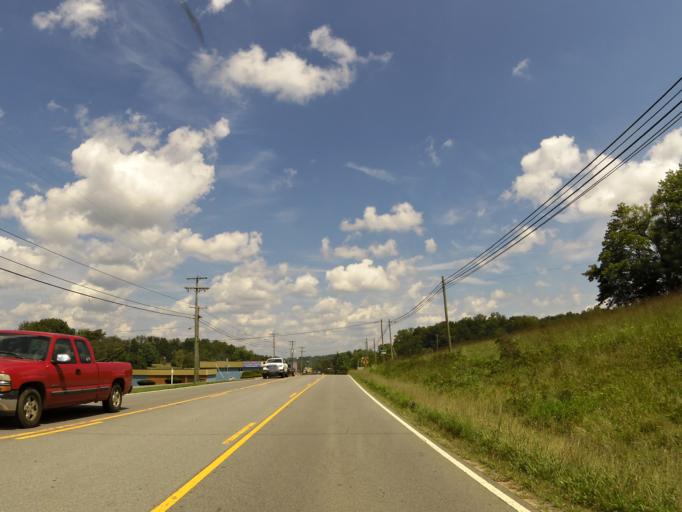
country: US
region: Virginia
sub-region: Washington County
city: Abingdon
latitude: 36.6734
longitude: -82.0513
